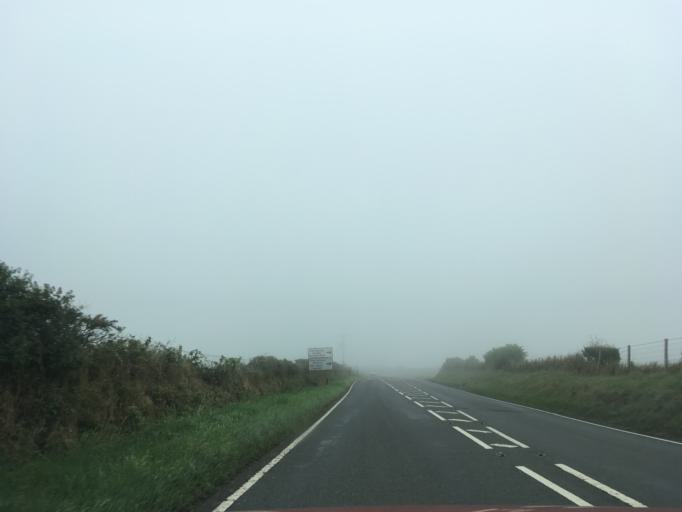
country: GB
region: Wales
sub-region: Pembrokeshire
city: Llanrhian
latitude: 51.8695
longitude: -5.1431
